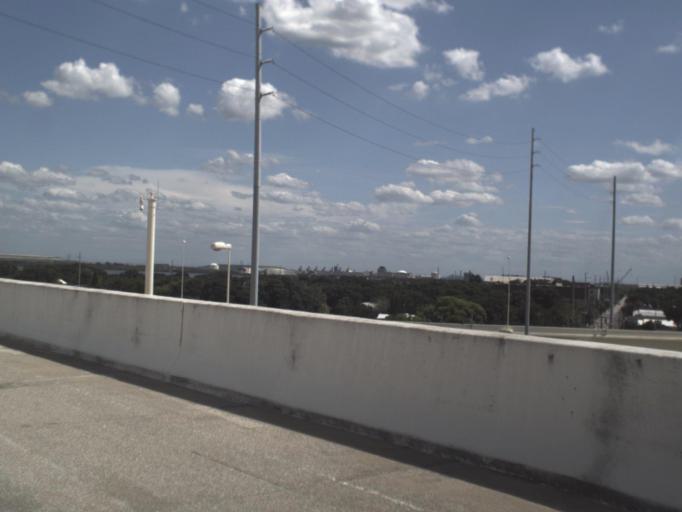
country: US
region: Florida
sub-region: Hillsborough County
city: Tampa
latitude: 27.9532
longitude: -82.4348
